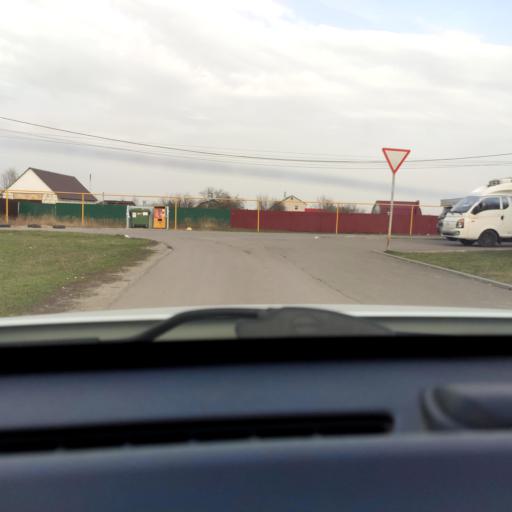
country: RU
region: Voronezj
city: Novaya Usman'
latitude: 51.6647
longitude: 39.3422
